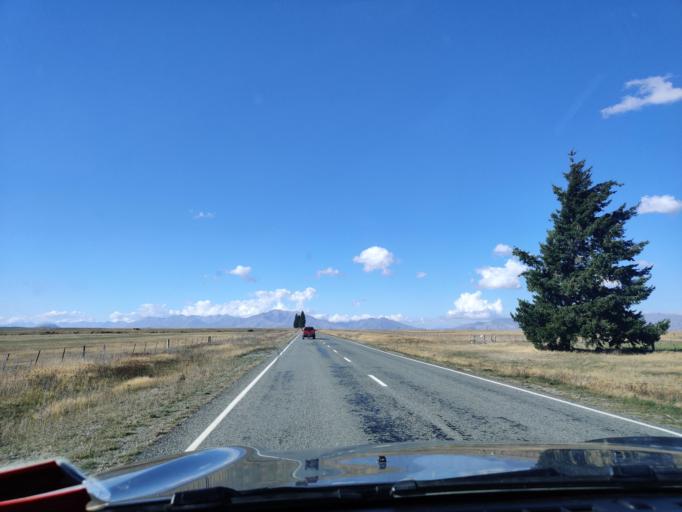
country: NZ
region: Canterbury
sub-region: Timaru District
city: Pleasant Point
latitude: -44.1729
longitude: 170.3266
